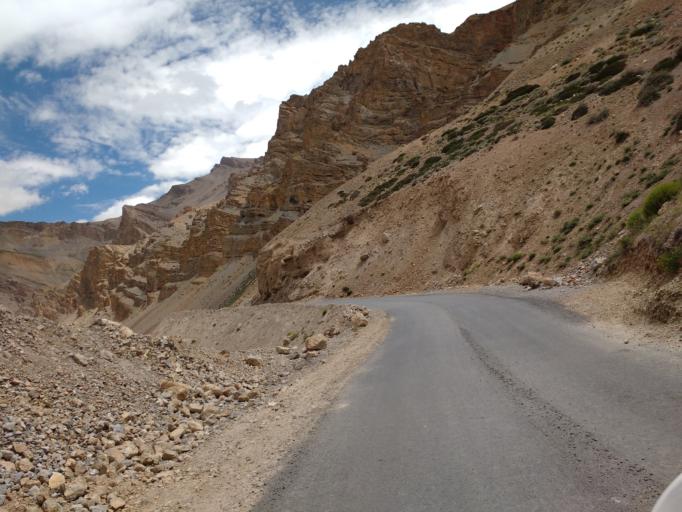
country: IN
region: Himachal Pradesh
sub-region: Lahul and Spiti
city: Kyelang
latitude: 33.0387
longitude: 77.5908
